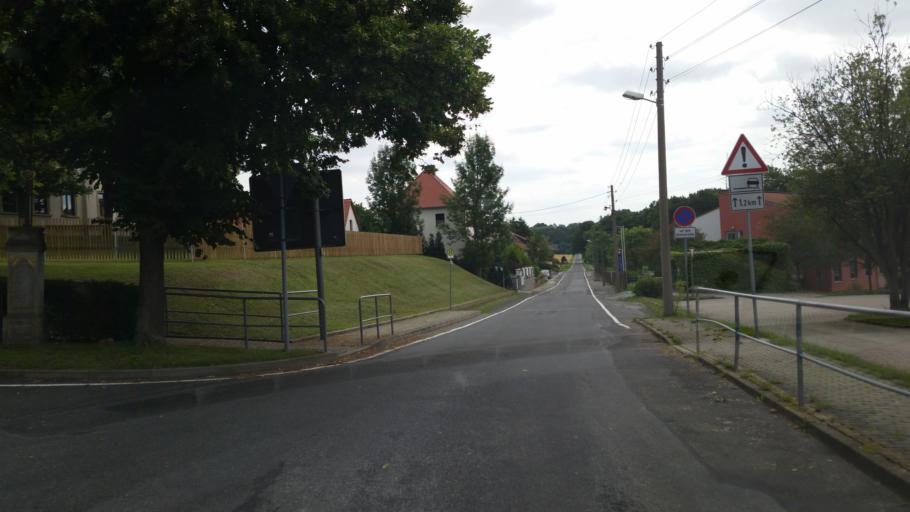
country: DE
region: Saxony
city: Crostwitz
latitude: 51.2381
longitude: 14.2487
